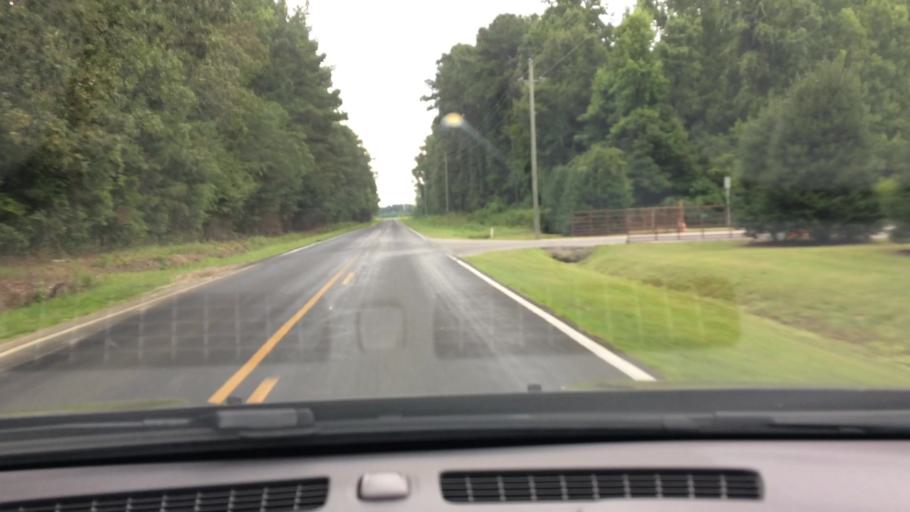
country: US
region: North Carolina
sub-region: Pitt County
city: Ayden
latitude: 35.4379
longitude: -77.4081
